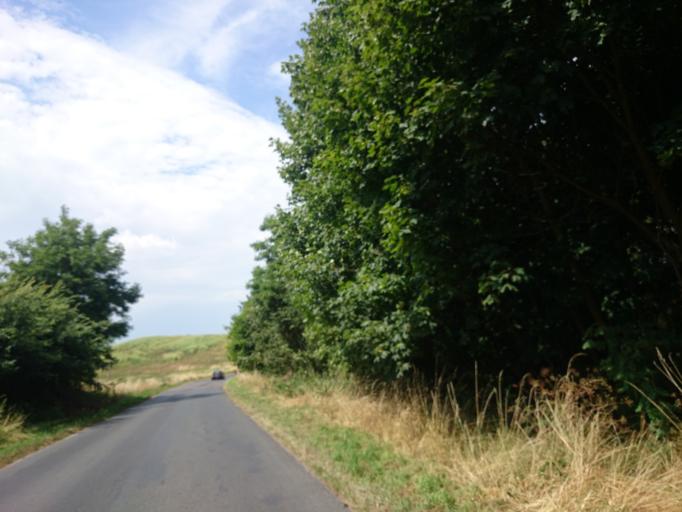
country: PL
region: West Pomeranian Voivodeship
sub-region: Powiat gryfinski
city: Moryn
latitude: 52.8683
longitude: 14.3805
